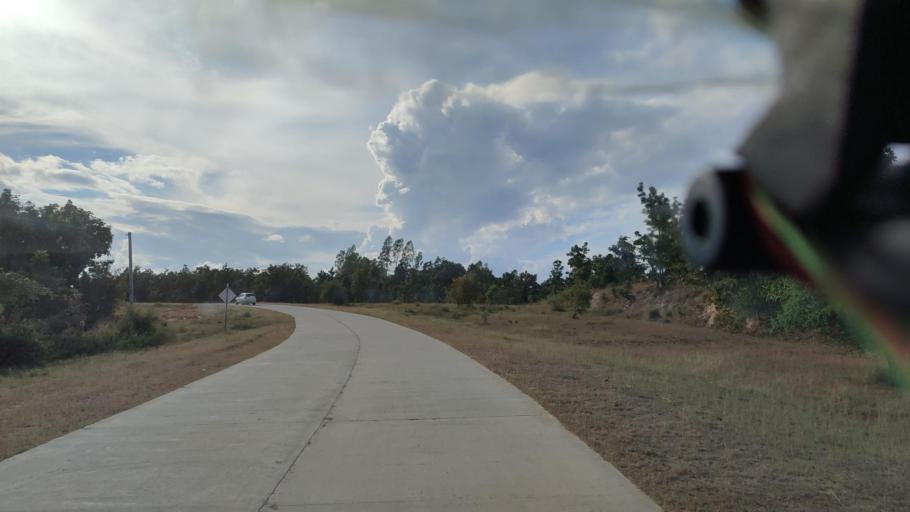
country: MM
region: Mandalay
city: Yamethin
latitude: 20.1234
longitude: 96.0595
